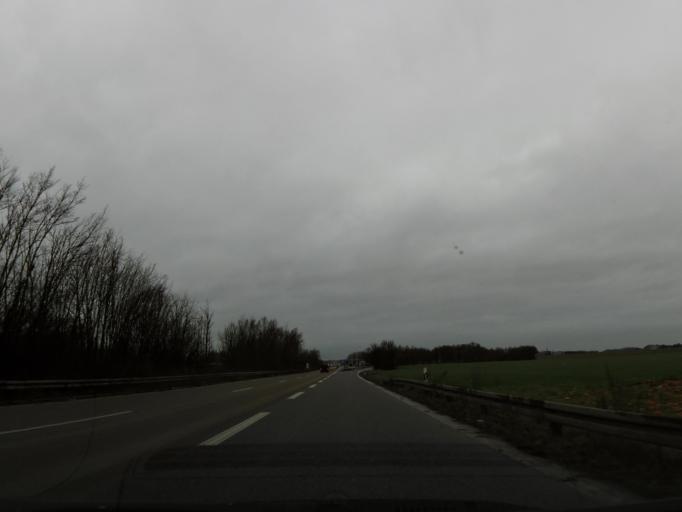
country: NL
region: Limburg
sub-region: Gemeente Vaals
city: Vaals
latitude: 50.8162
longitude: 6.0276
